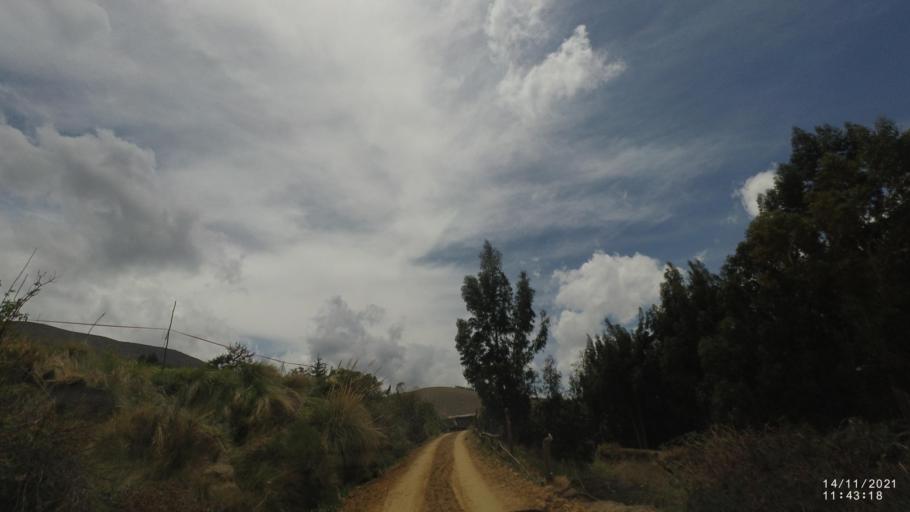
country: BO
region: Cochabamba
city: Colomi
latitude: -17.3520
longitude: -65.9919
